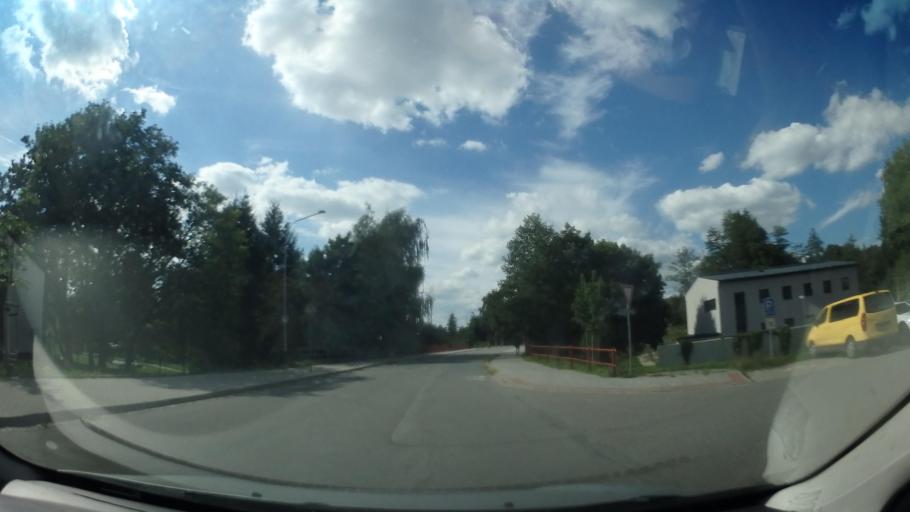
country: CZ
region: Vysocina
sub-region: Okres Zd'ar nad Sazavou
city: Zd'ar nad Sazavou
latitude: 49.5608
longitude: 15.9359
